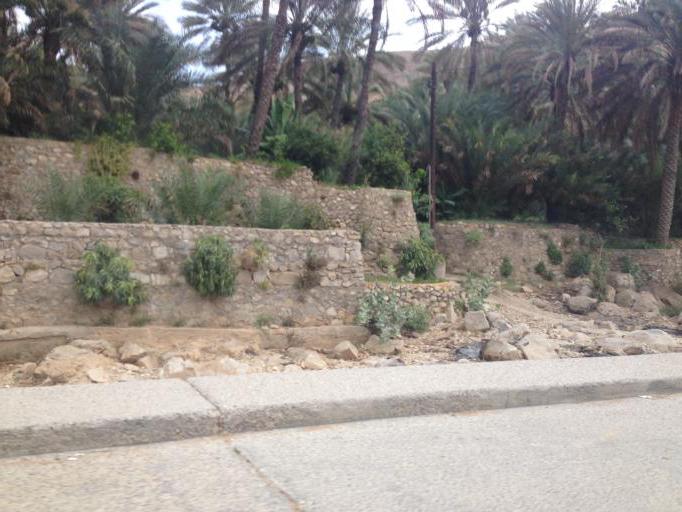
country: OM
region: Ash Sharqiyah
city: Badiyah
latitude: 22.6154
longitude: 59.0939
